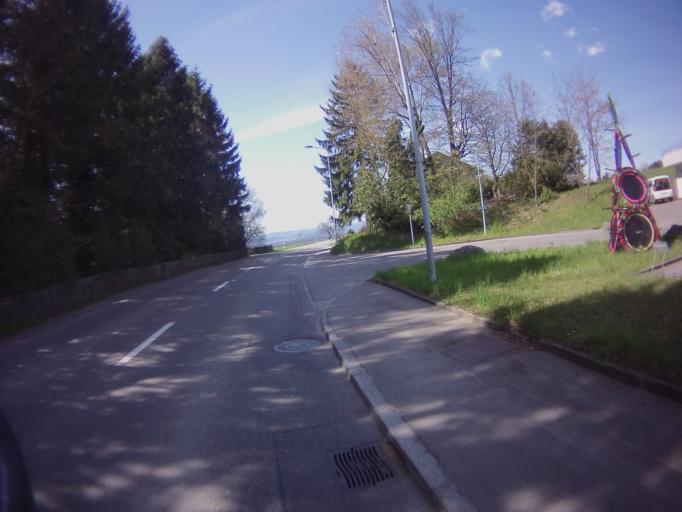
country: CH
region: Aargau
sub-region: Bezirk Baden
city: Kunten
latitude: 47.3910
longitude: 8.3426
